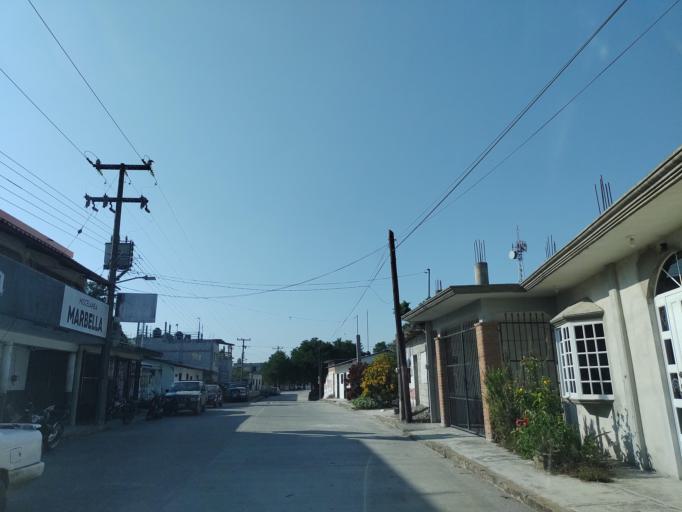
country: MX
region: Veracruz
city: Agua Dulce
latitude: 20.2533
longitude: -97.2547
